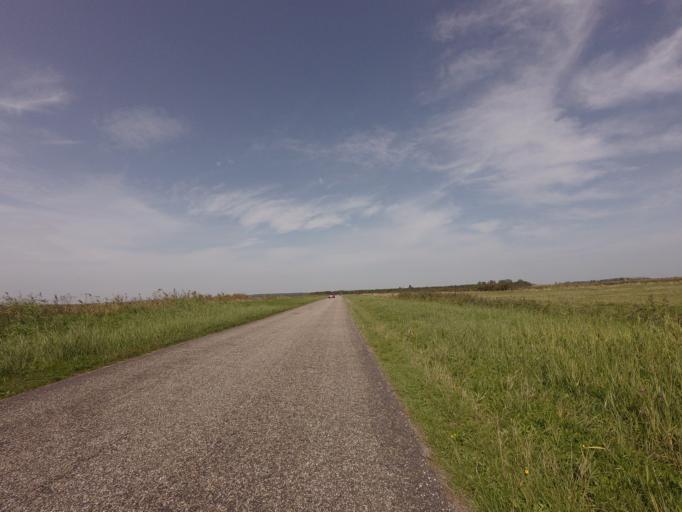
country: NL
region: Groningen
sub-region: Gemeente De Marne
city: Ulrum
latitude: 53.3506
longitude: 6.2662
